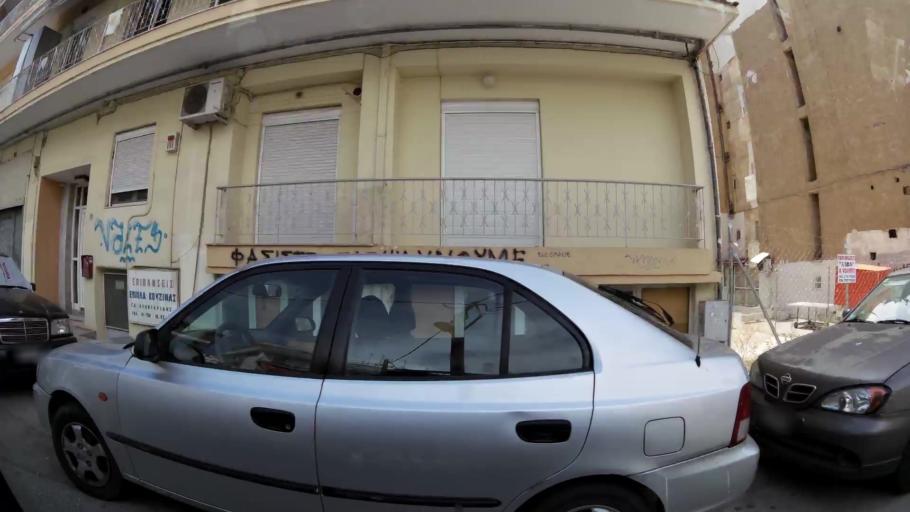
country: GR
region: Central Macedonia
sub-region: Nomos Thessalonikis
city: Triandria
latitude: 40.6041
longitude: 22.9623
